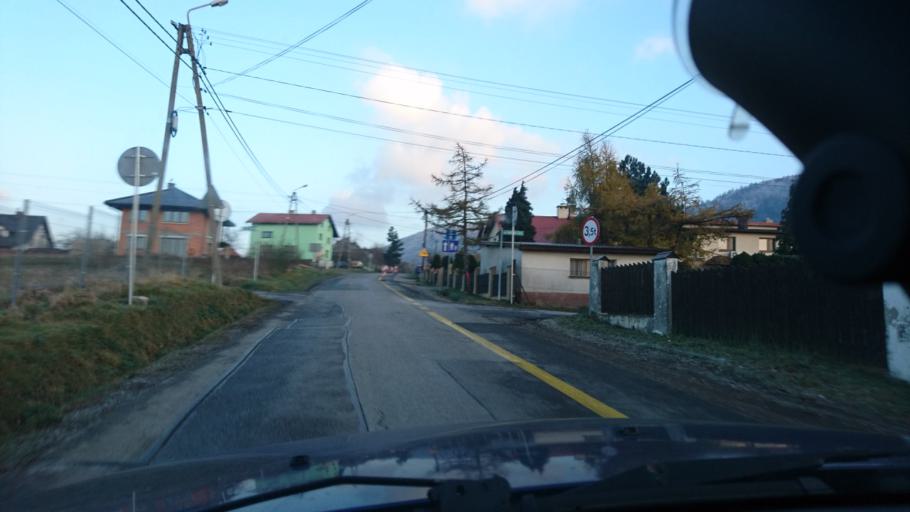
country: PL
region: Silesian Voivodeship
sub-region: Powiat bielski
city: Kozy
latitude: 49.8209
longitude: 19.1040
